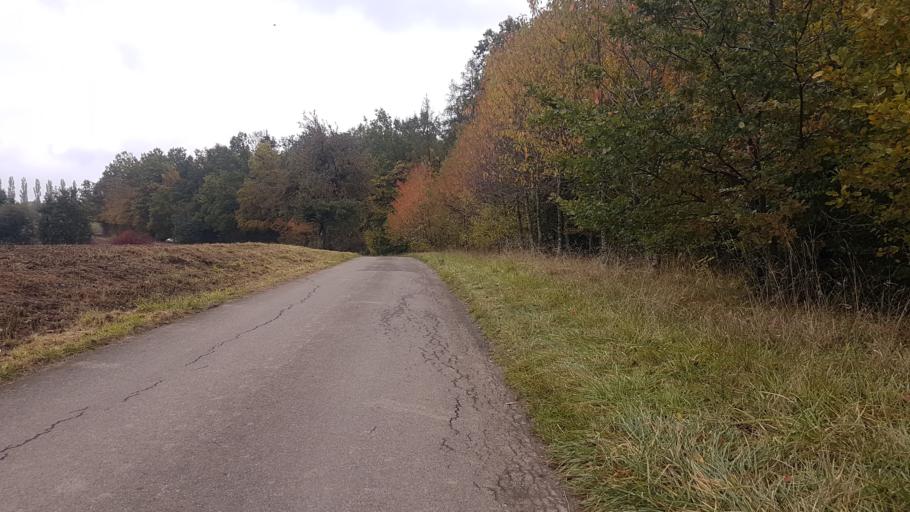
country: DE
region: Baden-Wuerttemberg
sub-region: Tuebingen Region
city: Dusslingen
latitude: 48.4647
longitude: 9.0395
